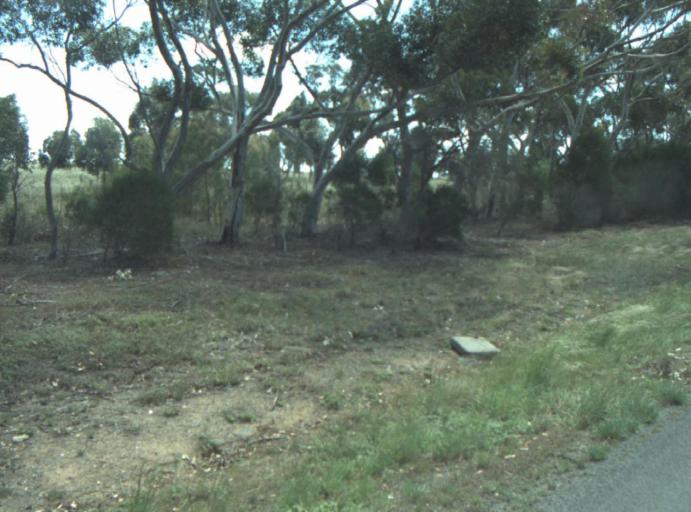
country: AU
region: Victoria
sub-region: Greater Geelong
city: Lara
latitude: -37.9629
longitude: 144.3507
